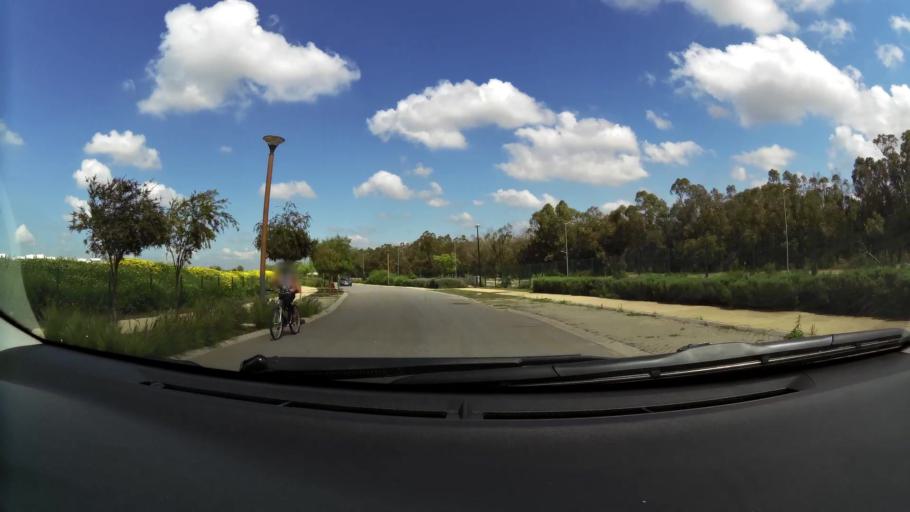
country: MA
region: Grand Casablanca
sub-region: Mediouna
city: Mediouna
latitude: 33.4840
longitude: -7.5825
